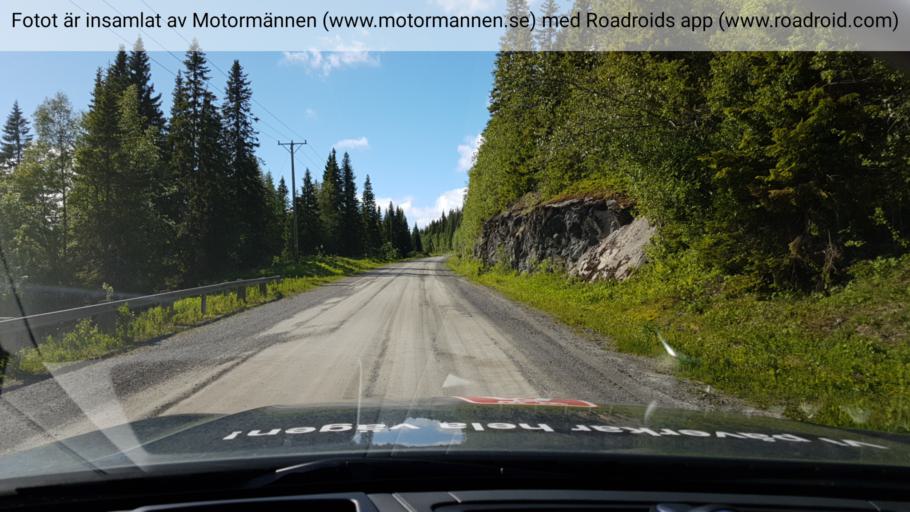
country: SE
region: Jaemtland
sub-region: Are Kommun
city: Are
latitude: 63.6949
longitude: 12.7935
